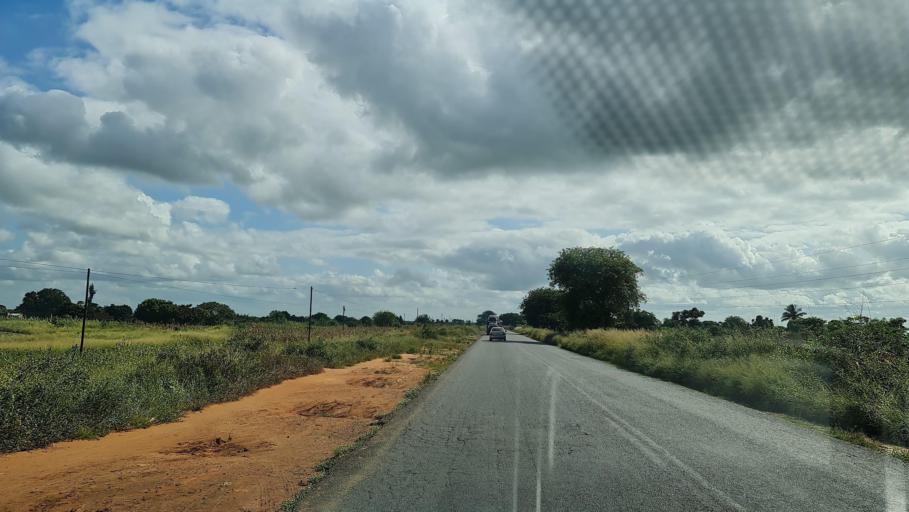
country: MZ
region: Gaza
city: Macia
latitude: -25.0845
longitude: 32.8462
